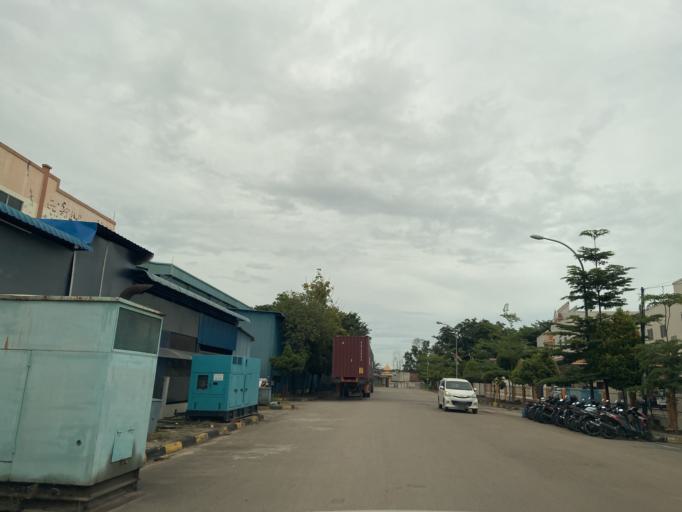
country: SG
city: Singapore
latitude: 1.1668
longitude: 104.0165
